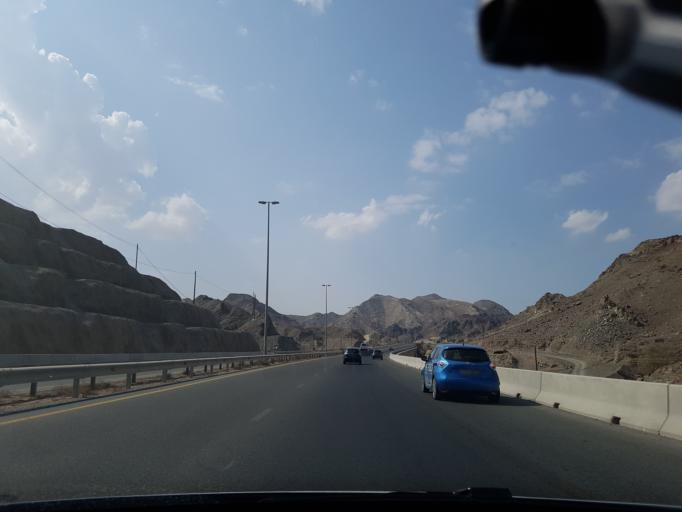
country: AE
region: Al Fujayrah
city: Dibba Al-Fujairah
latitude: 25.5303
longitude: 56.1392
